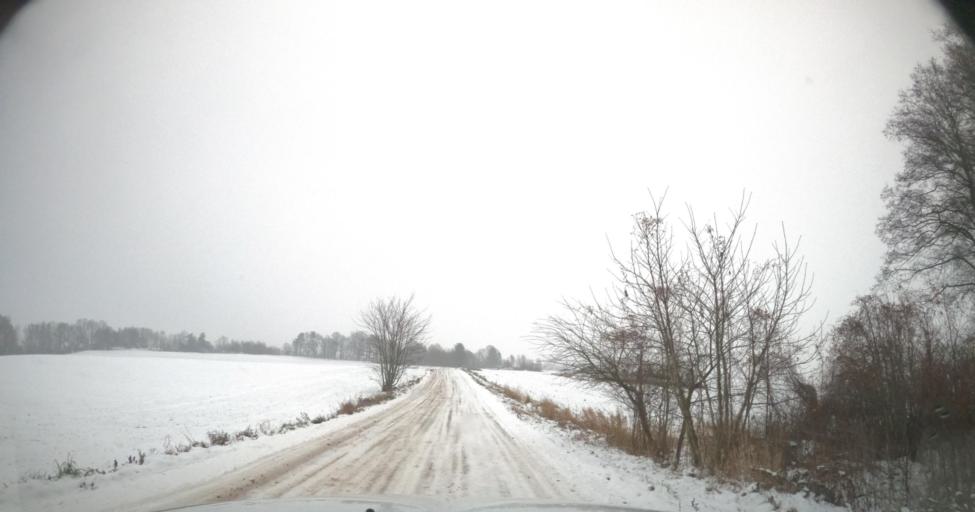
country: PL
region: West Pomeranian Voivodeship
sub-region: Powiat gryficki
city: Brojce
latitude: 53.9051
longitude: 15.3368
